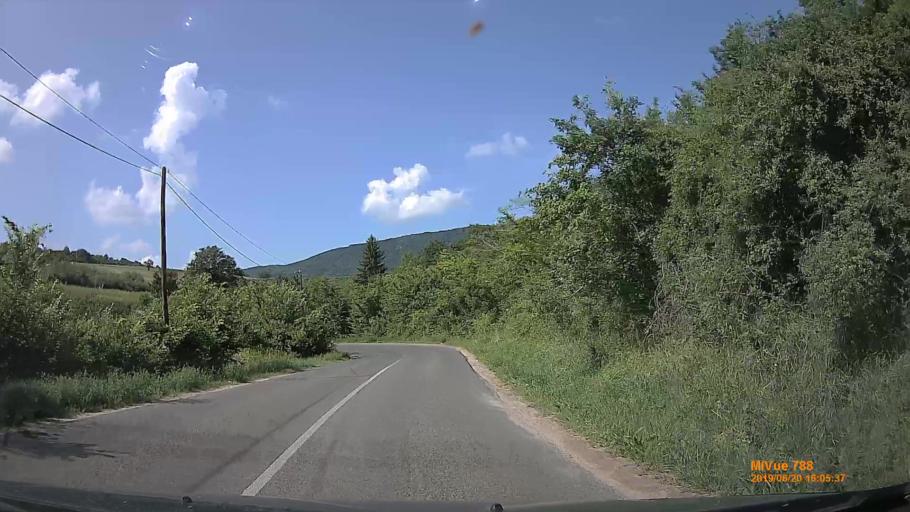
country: HU
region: Baranya
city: Pellerd
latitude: 46.0794
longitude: 18.1159
